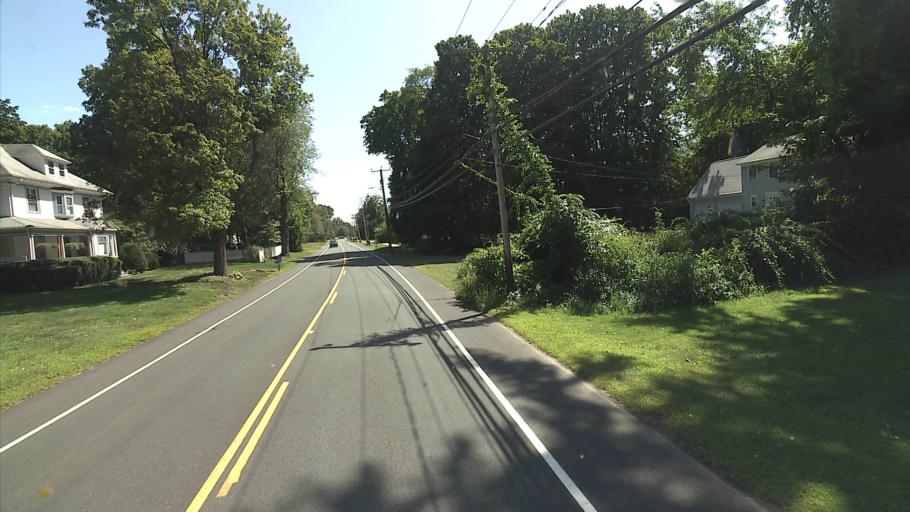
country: US
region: Connecticut
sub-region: Hartford County
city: Windsor
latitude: 41.8847
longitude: -72.6269
